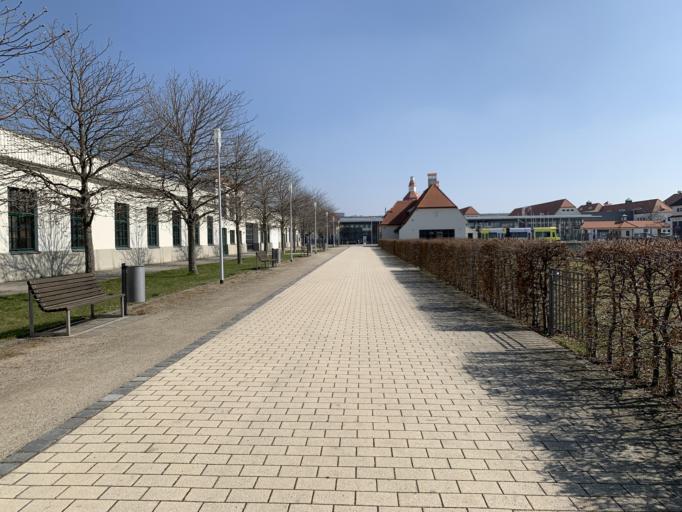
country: DE
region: Saxony
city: Dresden
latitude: 51.0704
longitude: 13.7127
